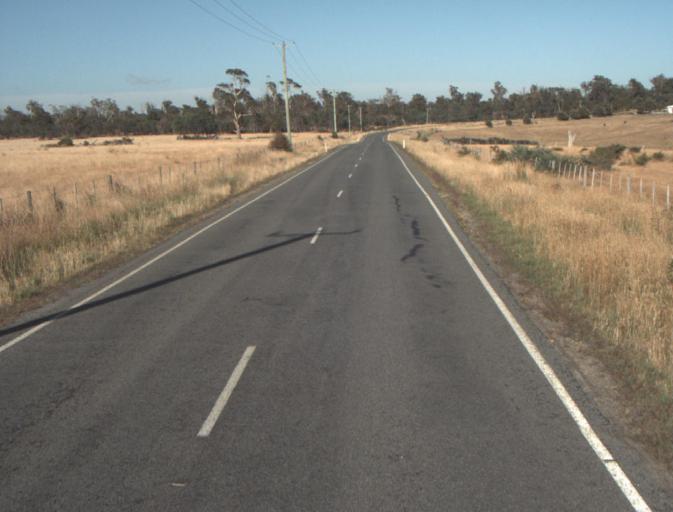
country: AU
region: Tasmania
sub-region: Launceston
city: Newstead
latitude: -41.4461
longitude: 147.2501
